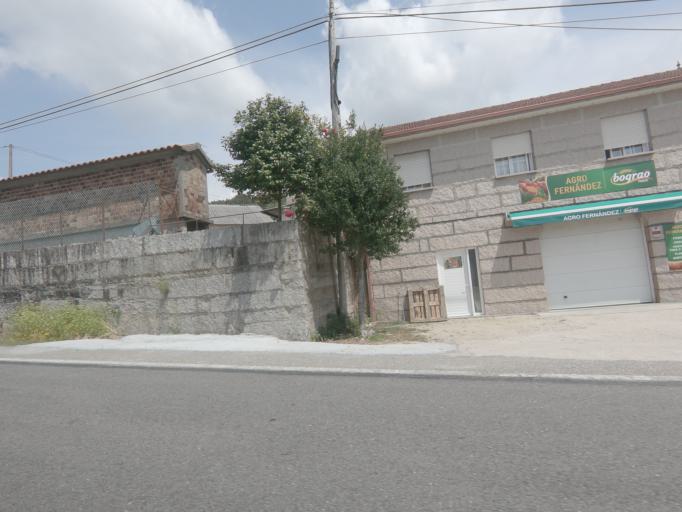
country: ES
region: Galicia
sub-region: Provincia de Pontevedra
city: Tomino
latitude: 42.0373
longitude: -8.7282
